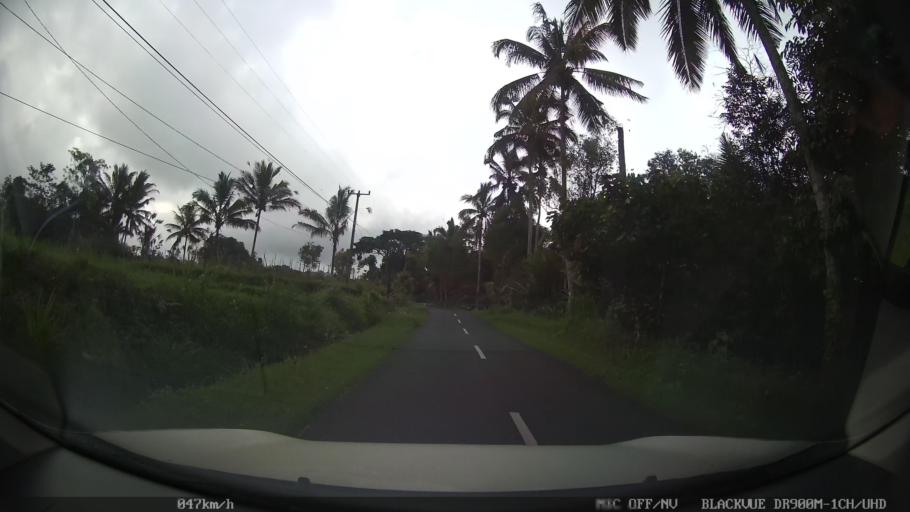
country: ID
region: Bali
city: Peneng
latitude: -8.3574
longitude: 115.2185
